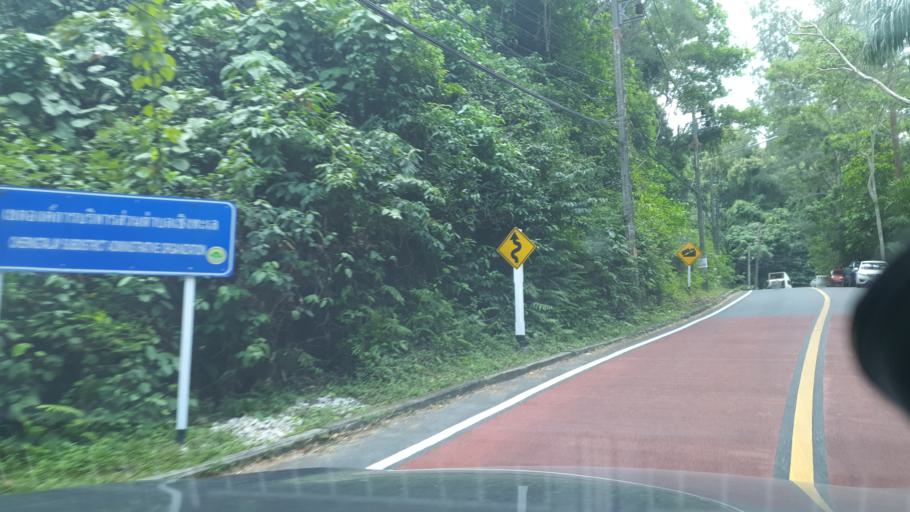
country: TH
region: Phuket
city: Thalang
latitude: 8.0430
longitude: 98.2783
